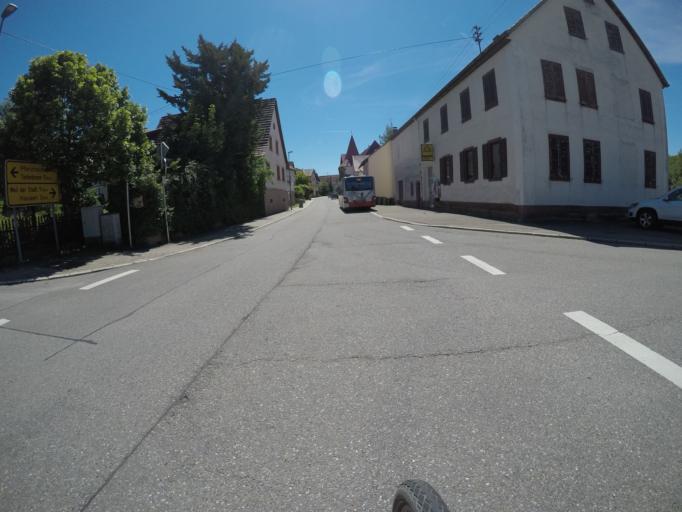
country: DE
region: Baden-Wuerttemberg
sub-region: Karlsruhe Region
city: Friolzheim
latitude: 48.8062
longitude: 8.8218
